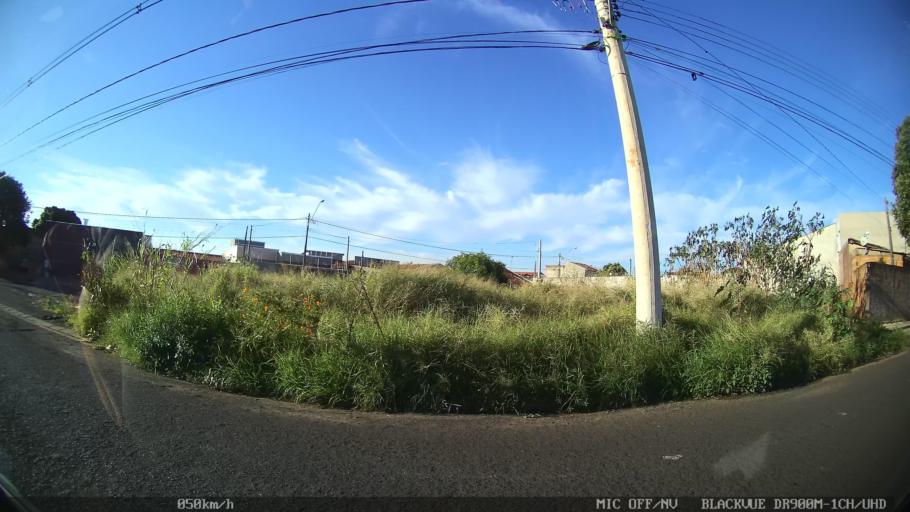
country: BR
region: Sao Paulo
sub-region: Americo Brasiliense
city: Americo Brasiliense
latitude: -21.7441
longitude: -48.1511
